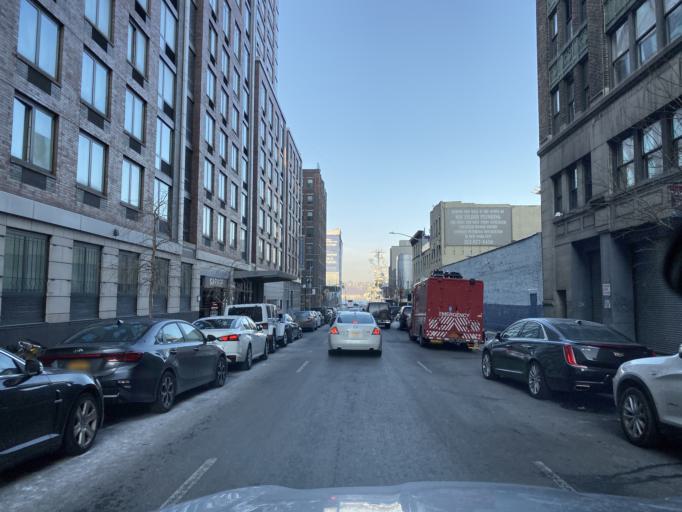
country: US
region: New Jersey
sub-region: Hudson County
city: Weehawken
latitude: 40.7623
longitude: -73.9958
